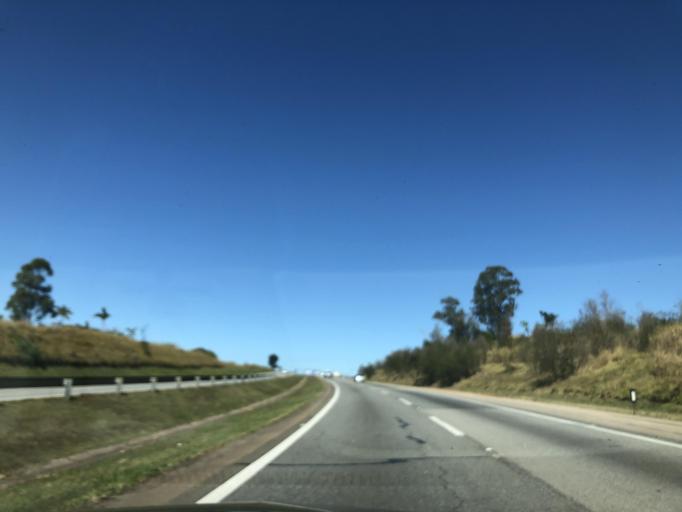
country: BR
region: Sao Paulo
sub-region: Sorocaba
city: Sorocaba
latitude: -23.4694
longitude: -47.3826
